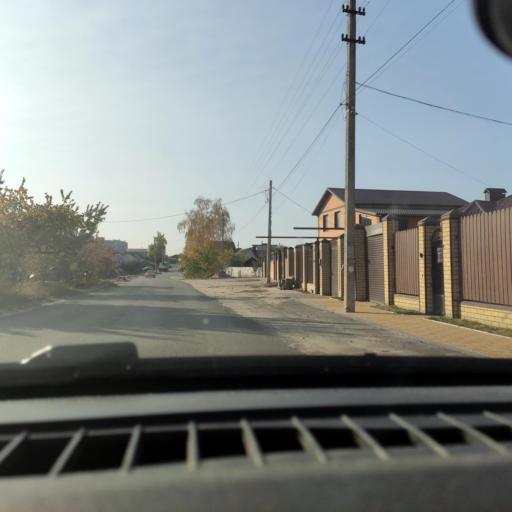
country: RU
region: Voronezj
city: Voronezh
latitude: 51.7034
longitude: 39.2709
